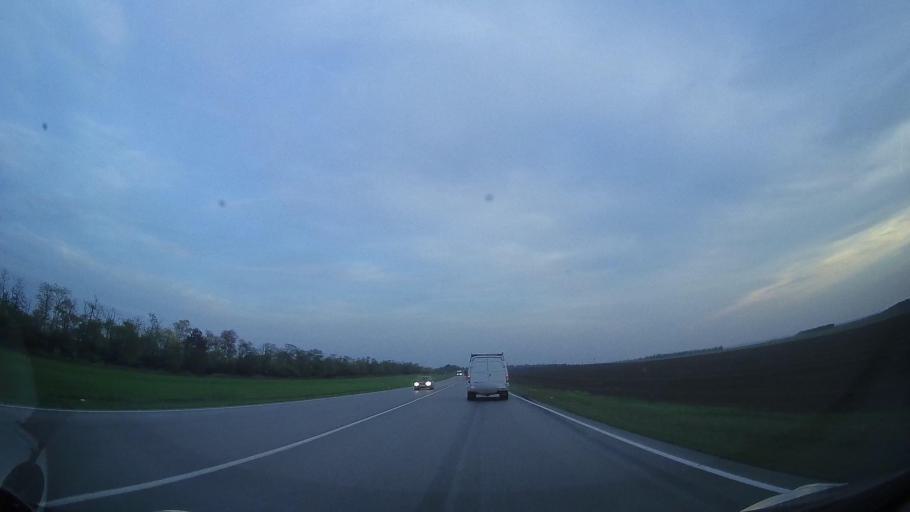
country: RU
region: Rostov
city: Kagal'nitskaya
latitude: 46.9016
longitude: 40.1222
